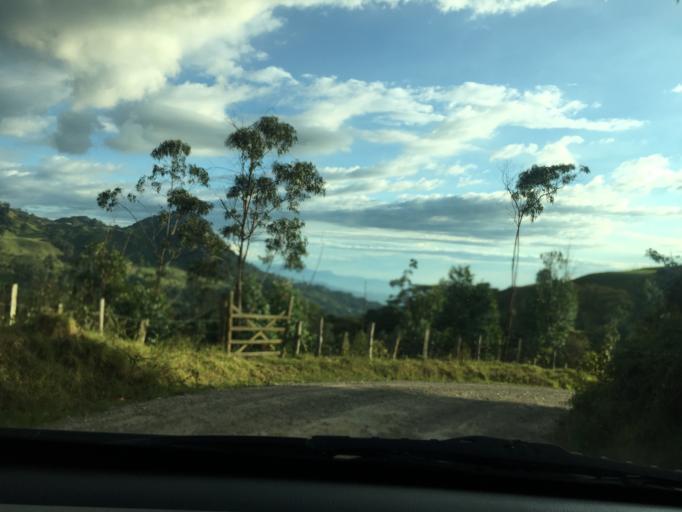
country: CO
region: Cundinamarca
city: Zipacon
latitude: 4.7313
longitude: -74.3902
